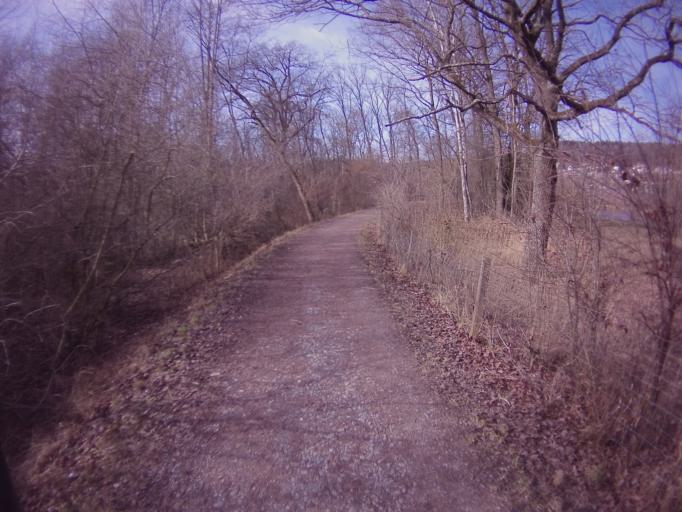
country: CH
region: Zurich
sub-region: Bezirk Dietikon
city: Geroldswil
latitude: 47.4183
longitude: 8.4038
